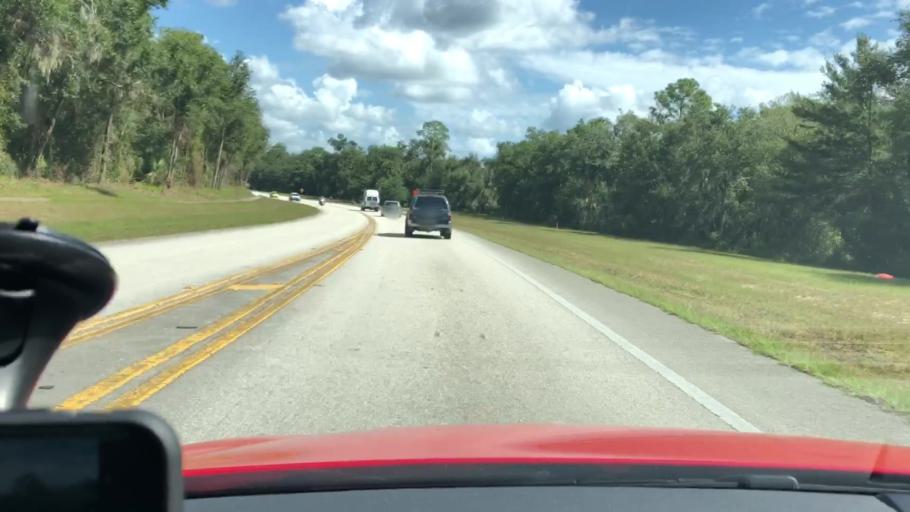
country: US
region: Florida
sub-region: Volusia County
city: Orange City
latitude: 28.9428
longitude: -81.2733
